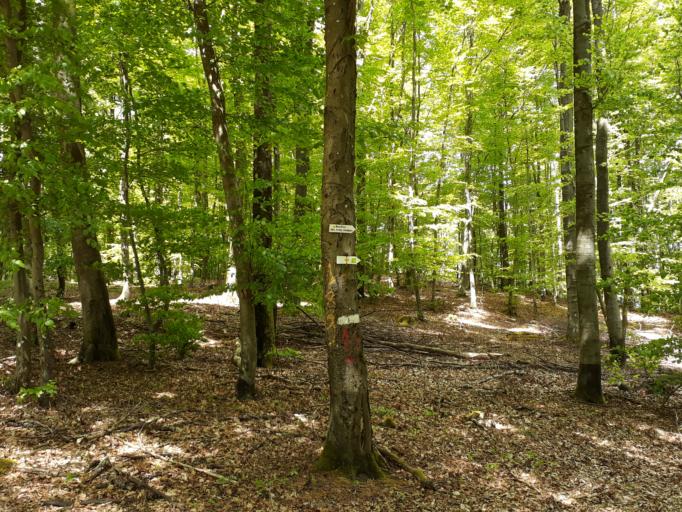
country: FR
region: Lorraine
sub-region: Departement de la Moselle
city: Phalsbourg
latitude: 48.8516
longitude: 7.2992
